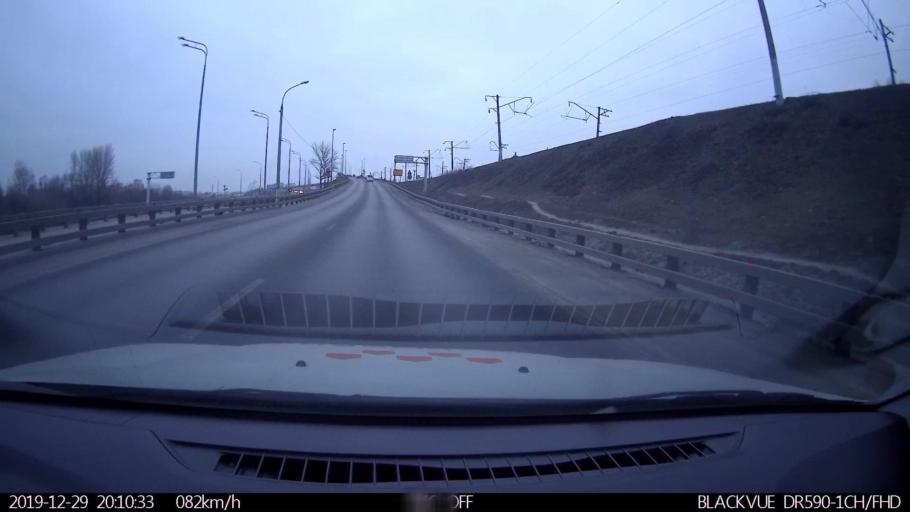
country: RU
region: Nizjnij Novgorod
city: Neklyudovo
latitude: 56.3647
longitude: 43.9353
